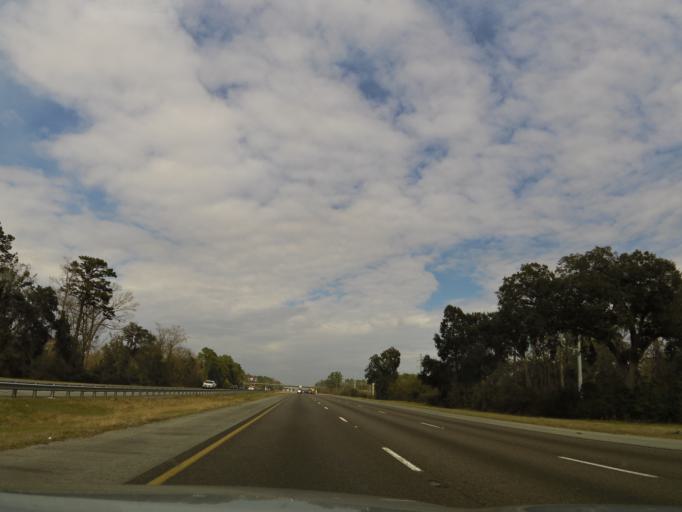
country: US
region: Georgia
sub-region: Liberty County
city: Midway
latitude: 31.8104
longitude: -81.3652
